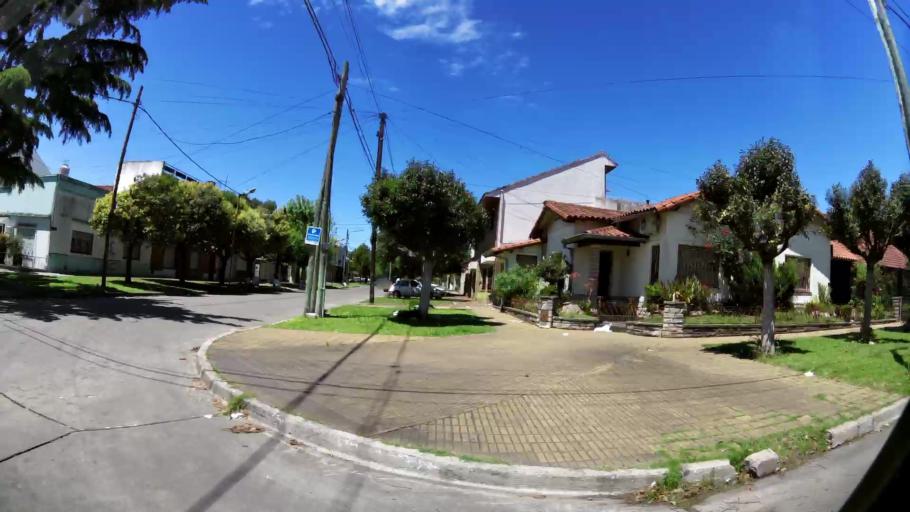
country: AR
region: Buenos Aires
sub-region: Partido de Quilmes
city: Quilmes
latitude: -34.7313
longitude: -58.2625
